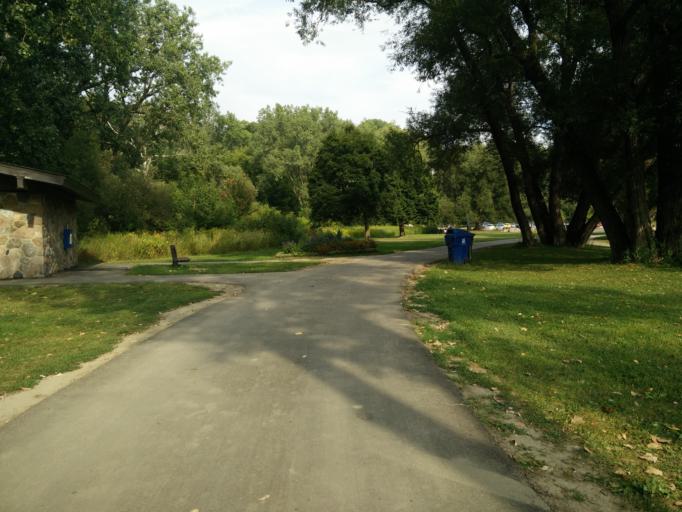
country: CA
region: Ontario
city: Etobicoke
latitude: 43.6528
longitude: -79.4931
